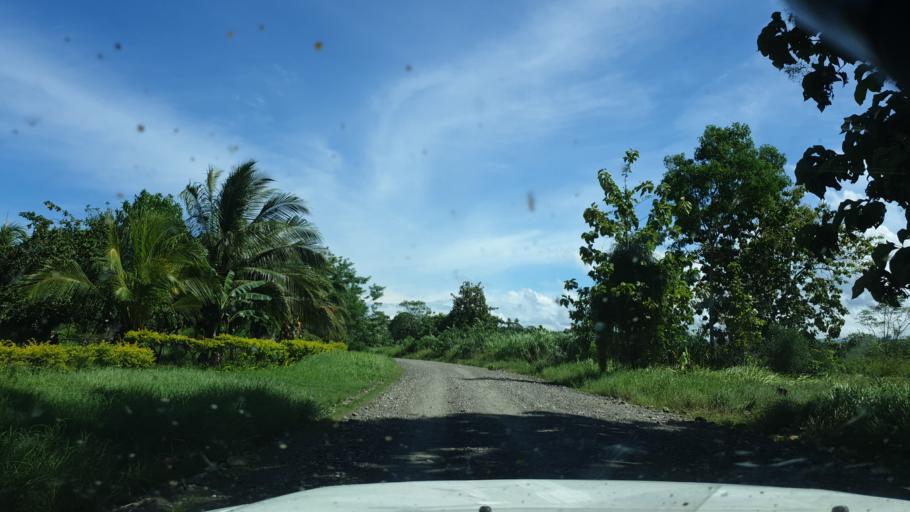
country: PG
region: Madang
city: Madang
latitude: -4.6302
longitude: 145.5636
